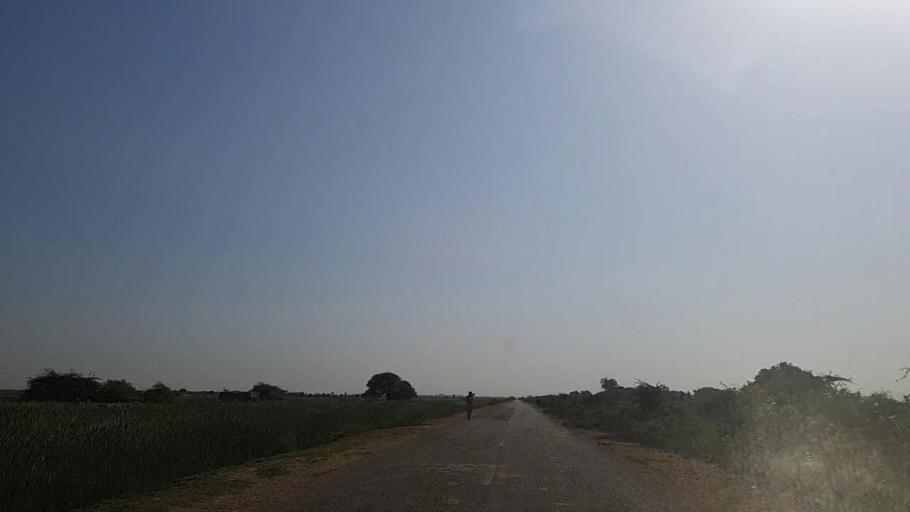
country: PK
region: Sindh
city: Jati
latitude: 24.4527
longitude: 68.2640
